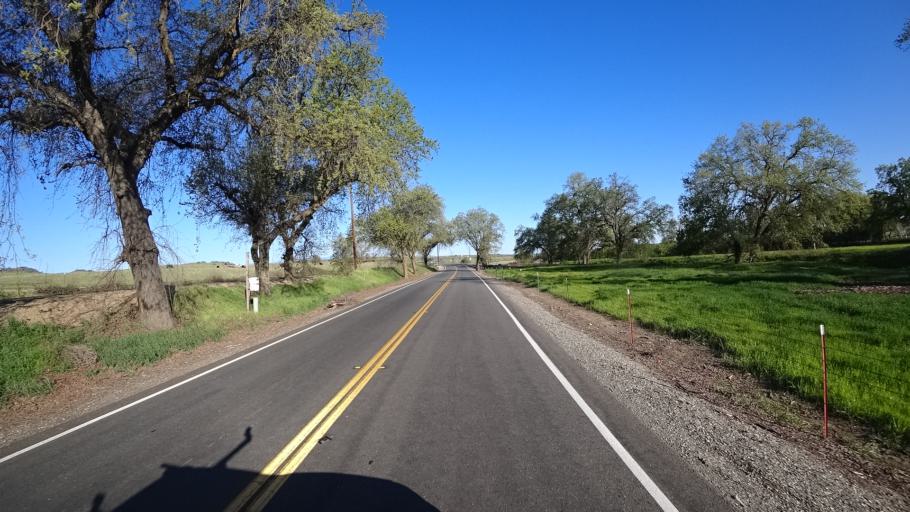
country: US
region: California
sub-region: Glenn County
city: Orland
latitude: 39.7979
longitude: -122.3186
